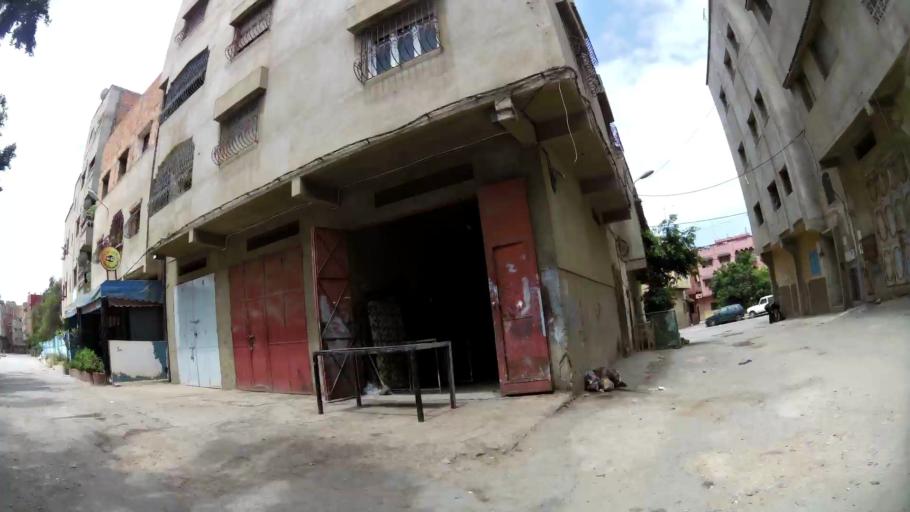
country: MA
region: Rabat-Sale-Zemmour-Zaer
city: Sale
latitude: 34.0575
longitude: -6.7812
